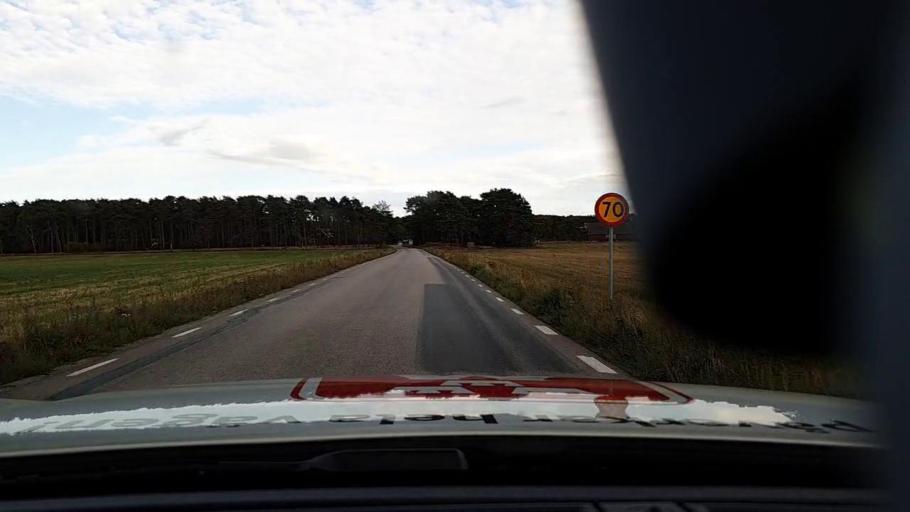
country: SE
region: Blekinge
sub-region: Solvesborgs Kommun
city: Soelvesborg
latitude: 56.0258
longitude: 14.7142
